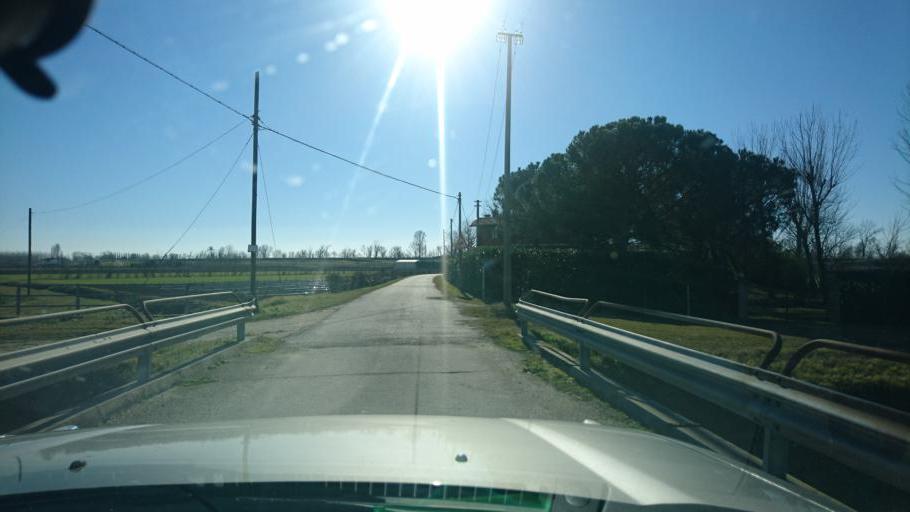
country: IT
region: Emilia-Romagna
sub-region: Provincia di Ferrara
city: Mesola
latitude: 44.9309
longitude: 12.2065
